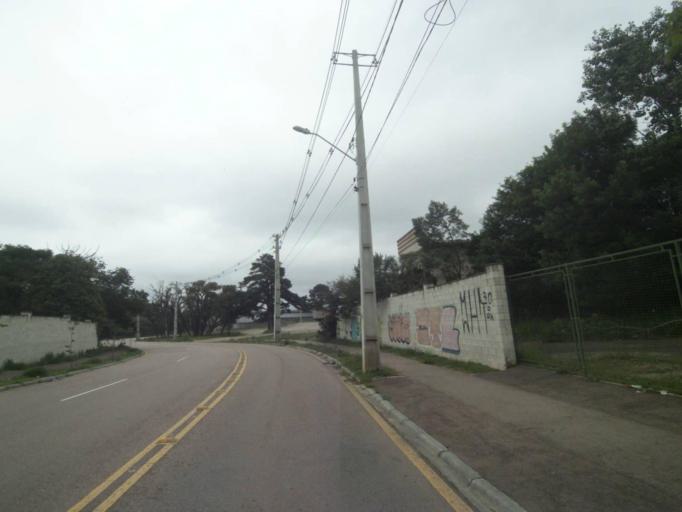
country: BR
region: Parana
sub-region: Sao Jose Dos Pinhais
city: Sao Jose dos Pinhais
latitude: -25.5535
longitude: -49.3072
